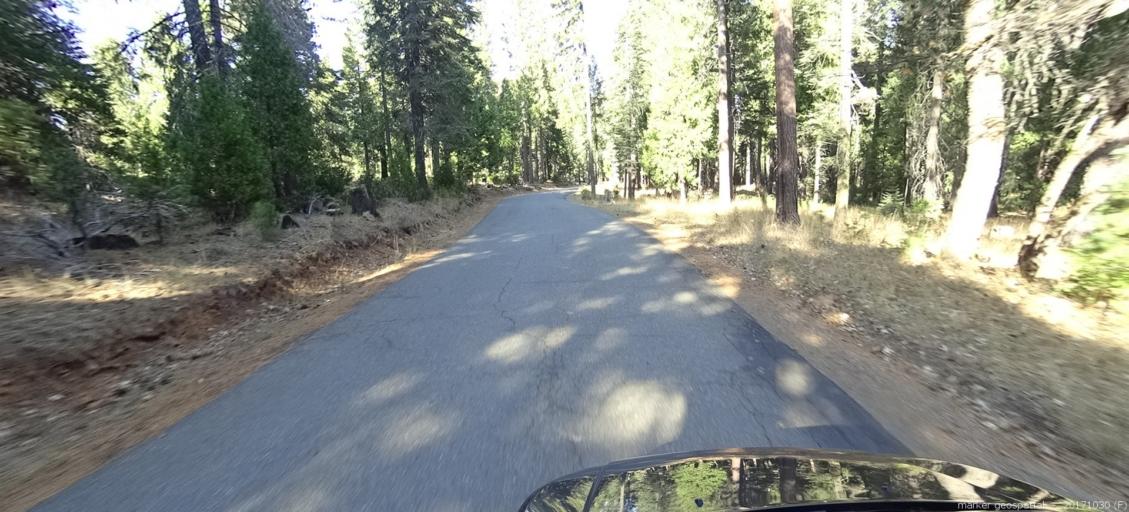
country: US
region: California
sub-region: Shasta County
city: Shingletown
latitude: 40.5403
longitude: -121.7372
